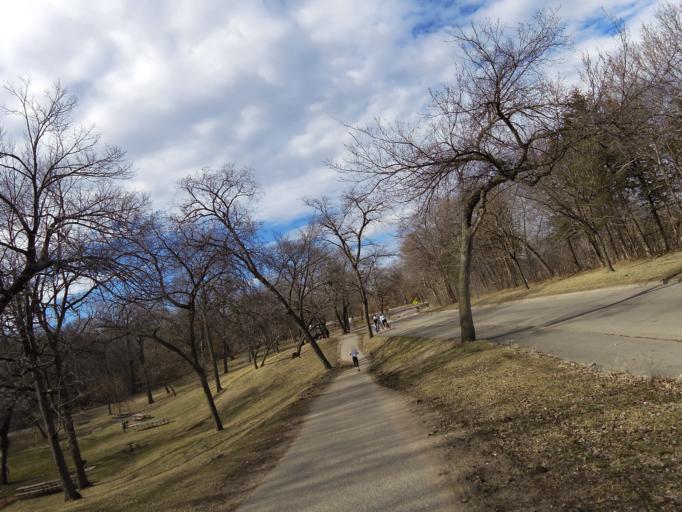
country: US
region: Minnesota
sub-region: Hennepin County
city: Saint Louis Park
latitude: 44.9296
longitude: -93.3078
